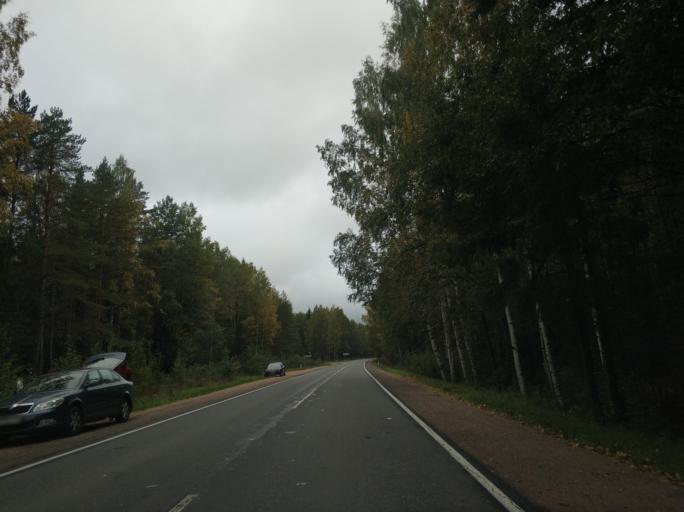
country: RU
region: Leningrad
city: Borisova Griva
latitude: 60.0893
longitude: 30.8643
